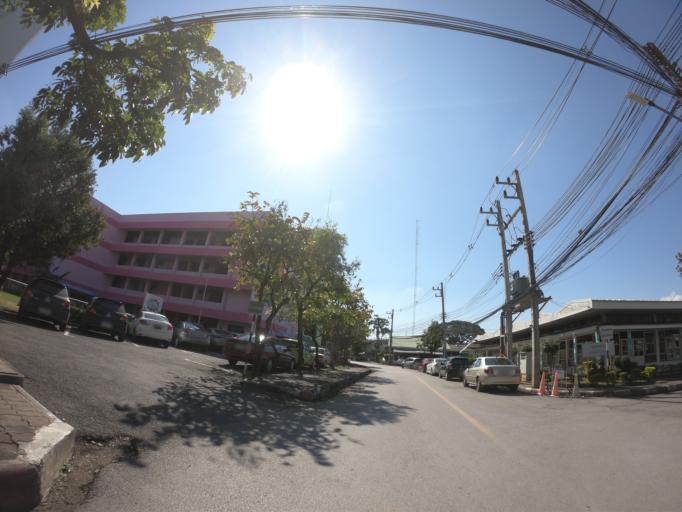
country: TH
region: Chiang Mai
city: Chiang Mai
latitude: 18.7726
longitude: 98.9952
